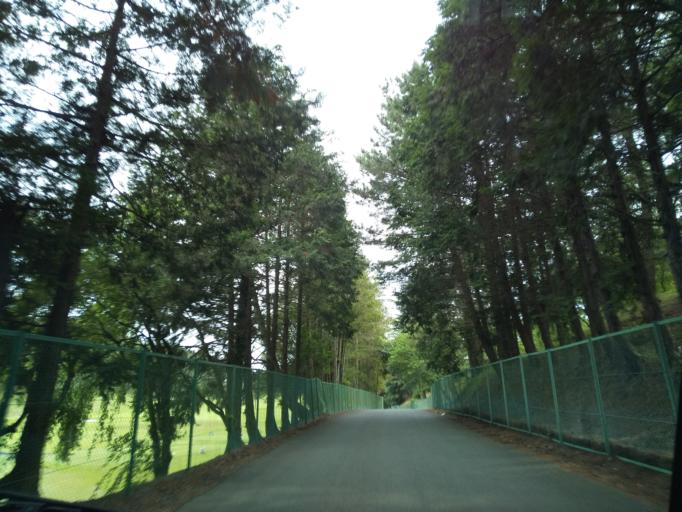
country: JP
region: Kanagawa
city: Atsugi
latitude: 35.4785
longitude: 139.3249
